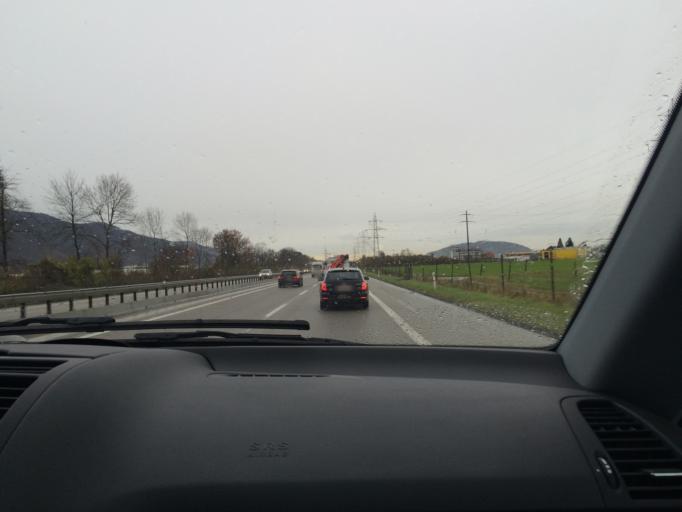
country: CH
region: Solothurn
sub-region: Bezirk Gaeu
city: Oberbuchsiten
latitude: 47.2991
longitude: 7.7626
